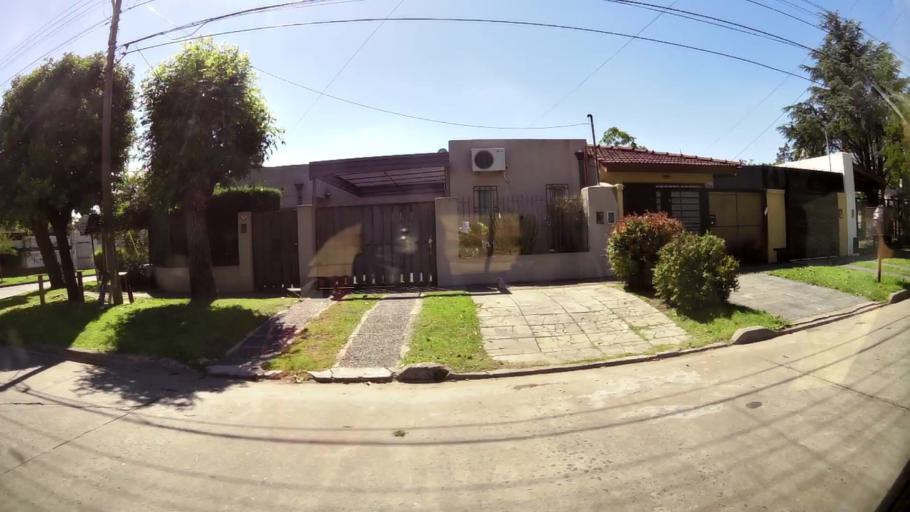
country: AR
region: Buenos Aires
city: Ituzaingo
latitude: -34.6414
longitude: -58.6611
